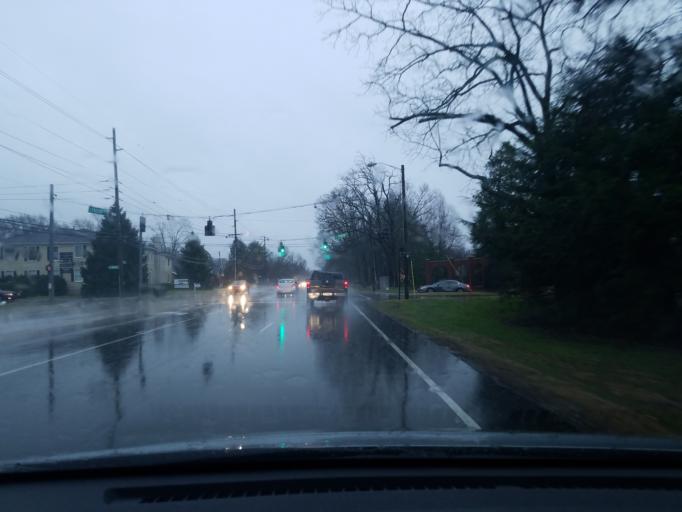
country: US
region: Kentucky
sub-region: Jefferson County
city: Lyndon
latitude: 38.2481
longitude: -85.5995
